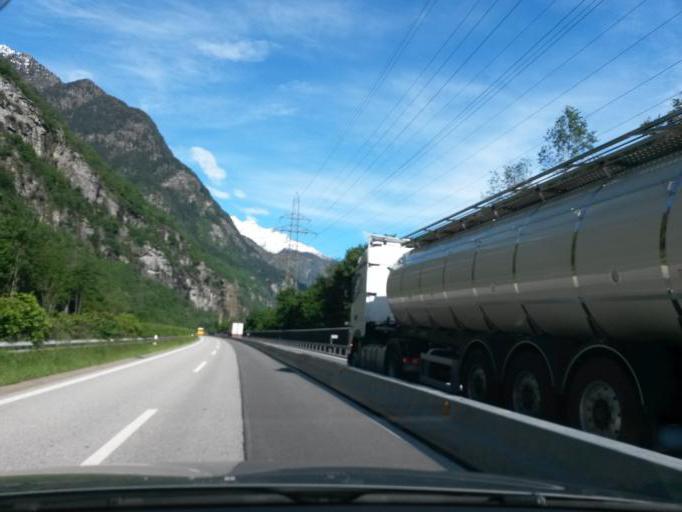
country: CH
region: Ticino
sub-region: Leventina District
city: Bodio
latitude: 46.3792
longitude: 8.9039
